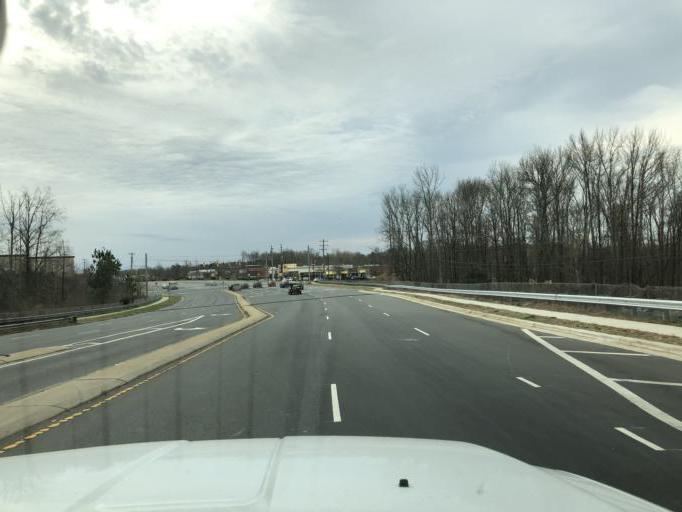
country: US
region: North Carolina
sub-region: Mecklenburg County
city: Huntersville
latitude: 35.3489
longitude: -80.8627
